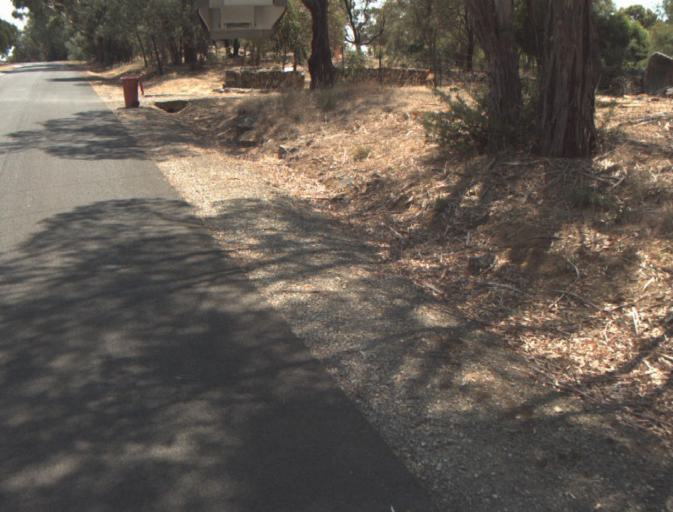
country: AU
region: Tasmania
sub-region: Launceston
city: Summerhill
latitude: -41.4891
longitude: 147.1801
